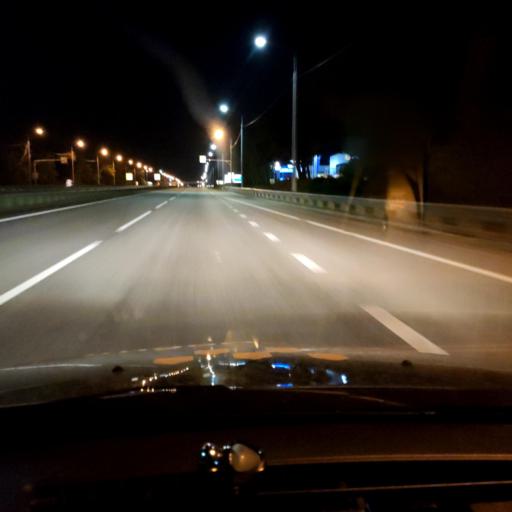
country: RU
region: Voronezj
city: Ramon'
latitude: 51.9354
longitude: 39.2211
